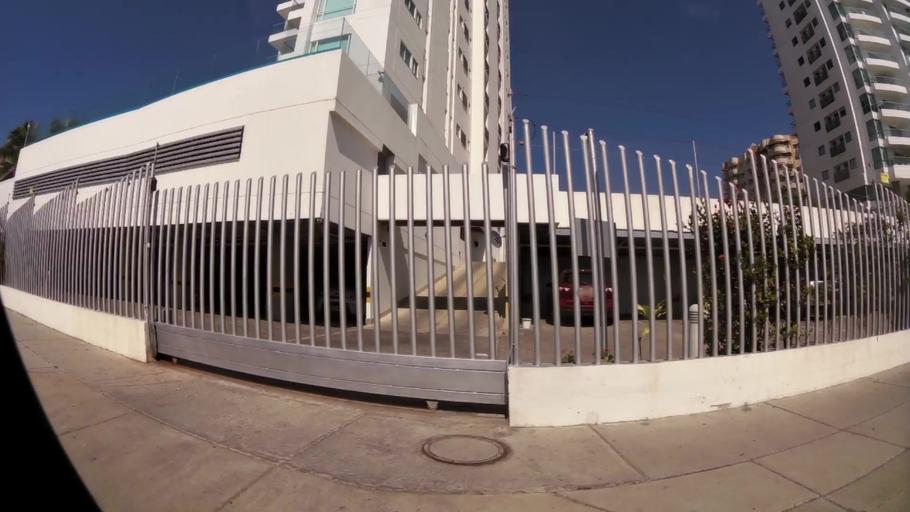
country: CO
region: Bolivar
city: Cartagena
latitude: 10.4316
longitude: -75.5421
